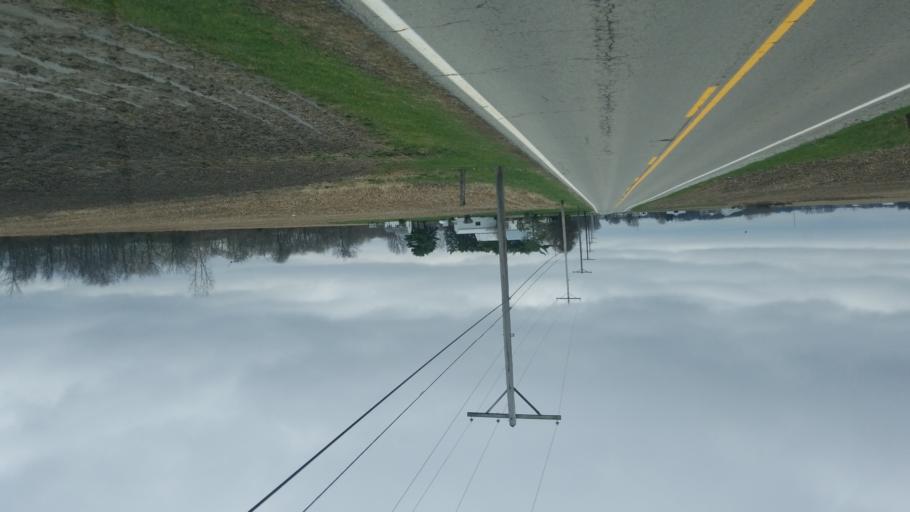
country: US
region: Ohio
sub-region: Hardin County
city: Kenton
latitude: 40.7064
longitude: -83.5713
